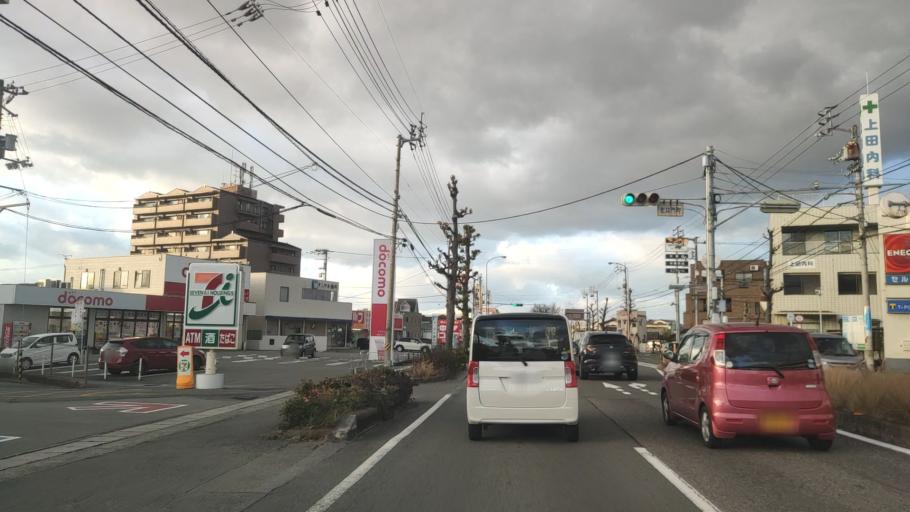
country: JP
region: Ehime
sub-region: Shikoku-chuo Shi
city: Matsuyama
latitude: 33.8041
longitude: 132.7825
